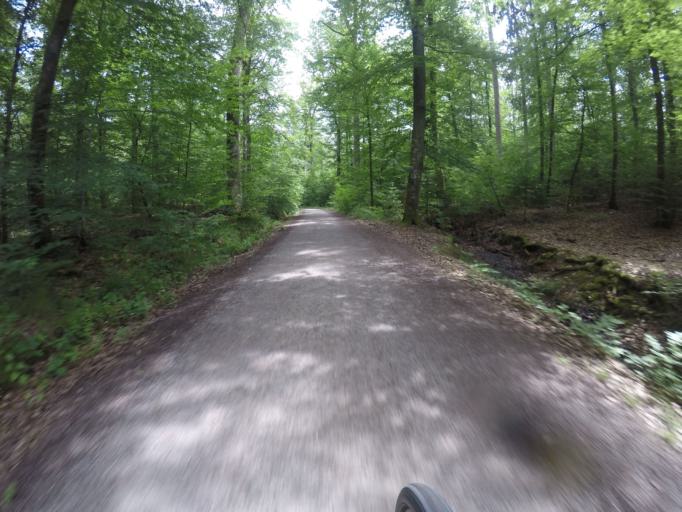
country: DE
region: Baden-Wuerttemberg
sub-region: Regierungsbezirk Stuttgart
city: Nufringen
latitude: 48.5983
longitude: 8.9112
